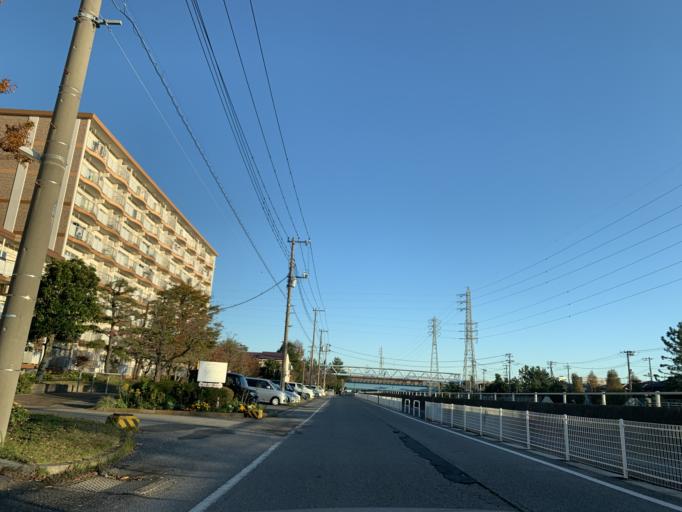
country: JP
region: Tokyo
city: Urayasu
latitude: 35.6607
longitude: 139.9106
